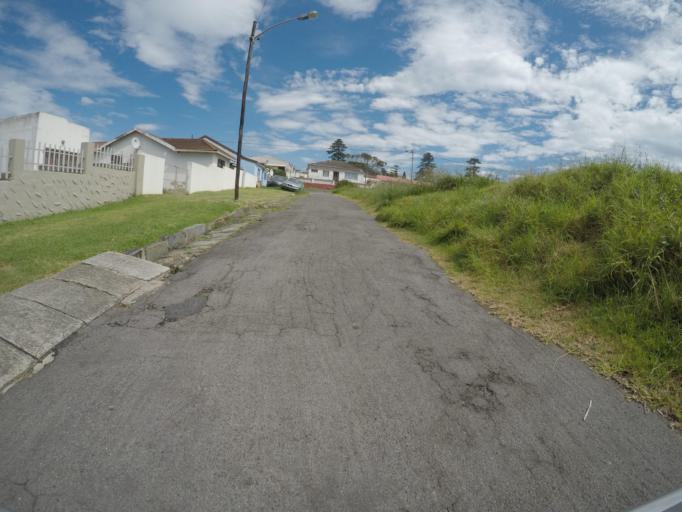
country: ZA
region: Eastern Cape
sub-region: Buffalo City Metropolitan Municipality
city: East London
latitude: -33.0326
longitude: 27.9105
